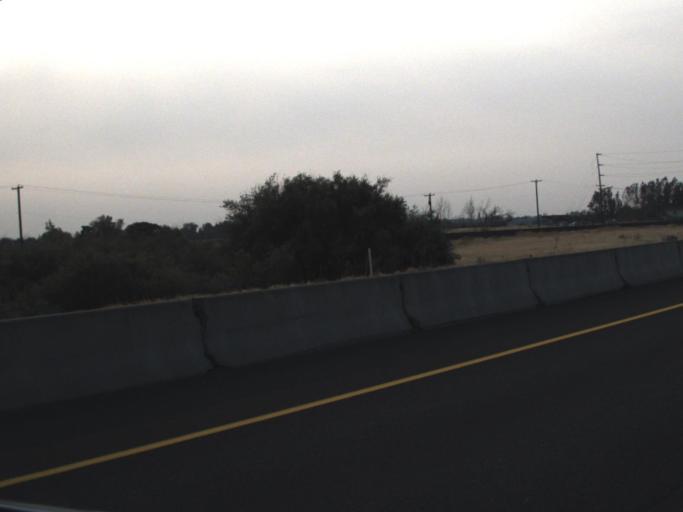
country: US
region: Washington
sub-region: Yakima County
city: Wapato
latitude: 46.4940
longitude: -120.4598
